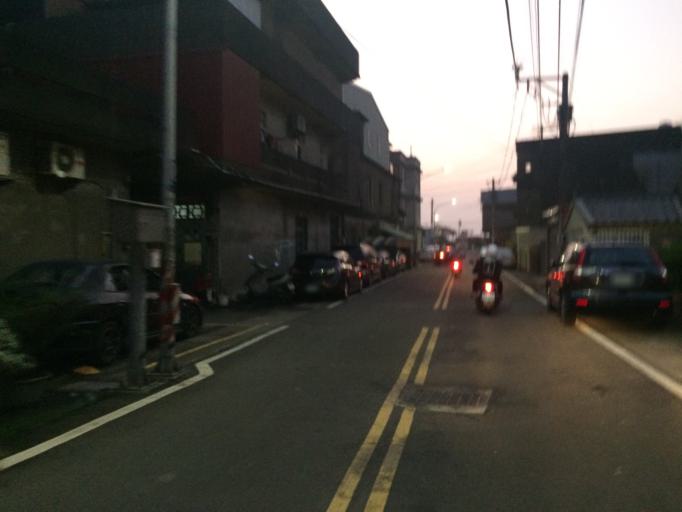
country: TW
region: Taiwan
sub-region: Hsinchu
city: Hsinchu
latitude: 24.7744
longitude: 120.9160
